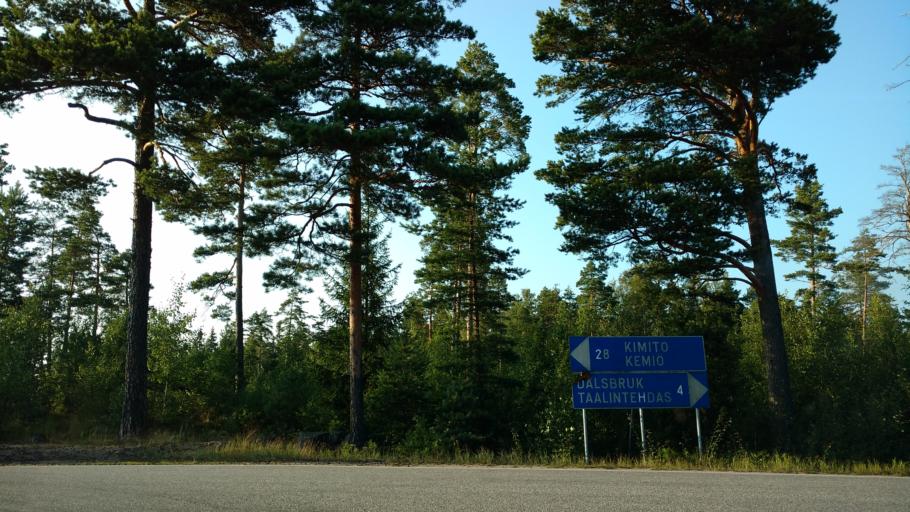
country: FI
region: Varsinais-Suomi
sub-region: Aboland-Turunmaa
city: Dragsfjaerd
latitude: 60.0281
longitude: 22.4613
